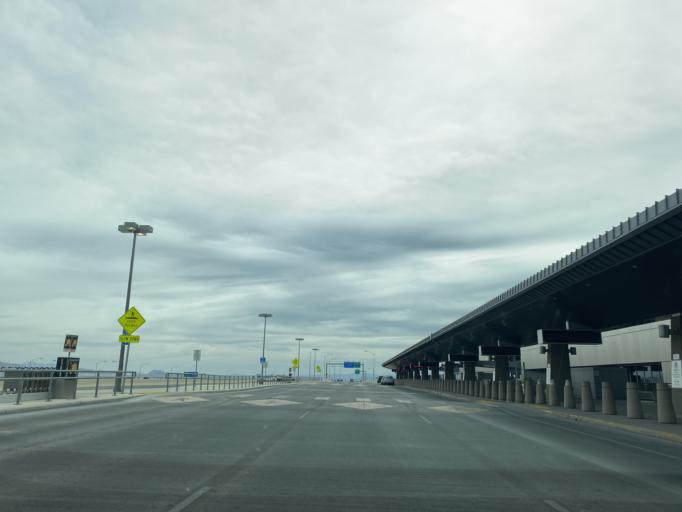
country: US
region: Nevada
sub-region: Clark County
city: Paradise
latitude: 36.0868
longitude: -115.1372
